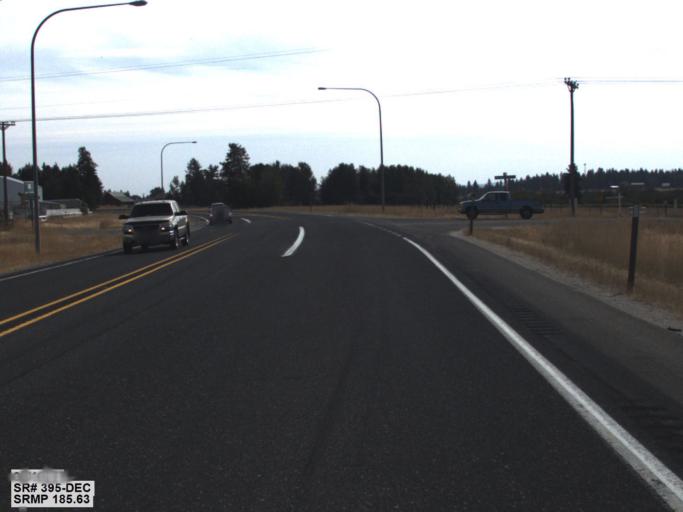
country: US
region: Washington
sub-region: Spokane County
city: Deer Park
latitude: 47.9974
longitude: -117.5727
